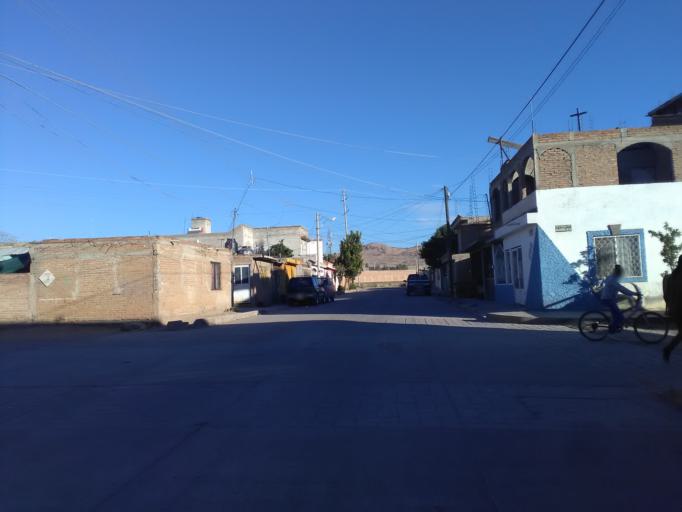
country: MX
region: Durango
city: Victoria de Durango
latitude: 24.0540
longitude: -104.6541
